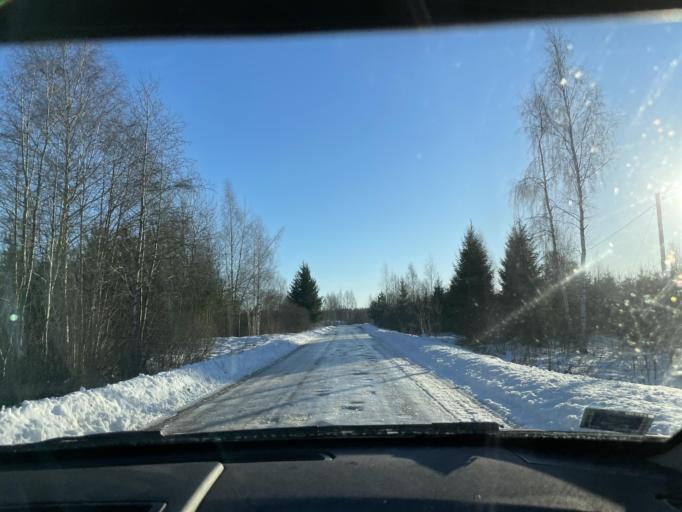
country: LV
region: Ludzas Rajons
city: Ludza
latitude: 56.4623
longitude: 27.6073
